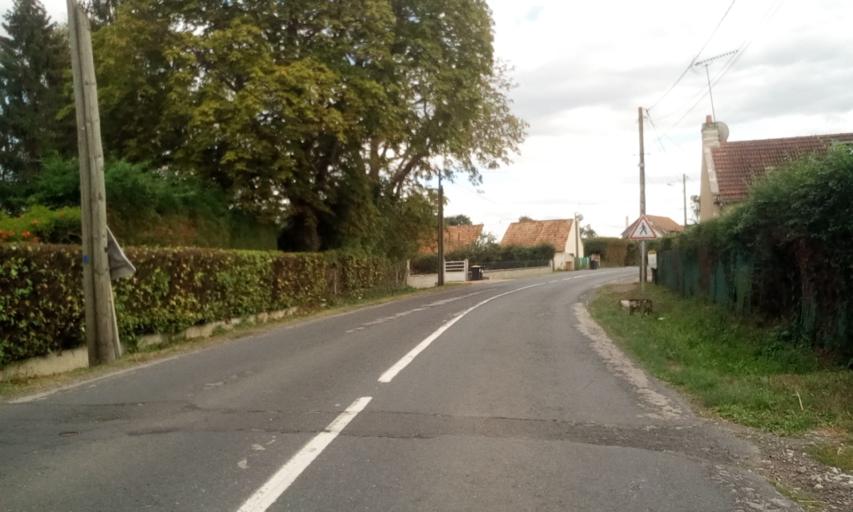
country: FR
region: Lower Normandy
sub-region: Departement du Calvados
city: Troarn
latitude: 49.1650
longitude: -0.1810
